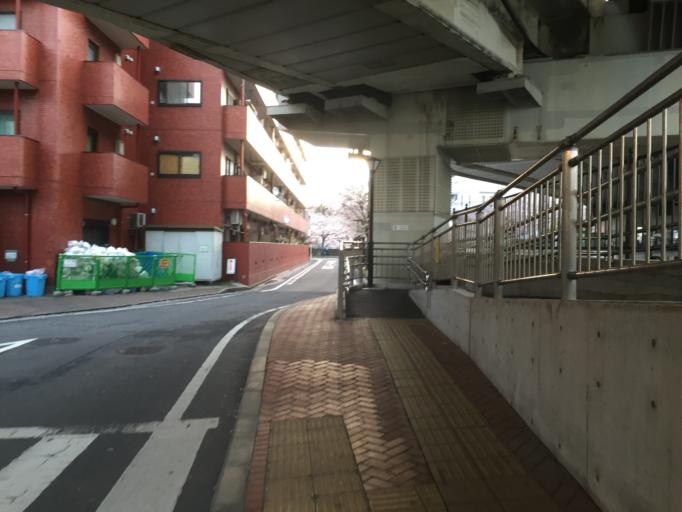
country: JP
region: Kanagawa
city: Yokohama
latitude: 35.4352
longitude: 139.6137
